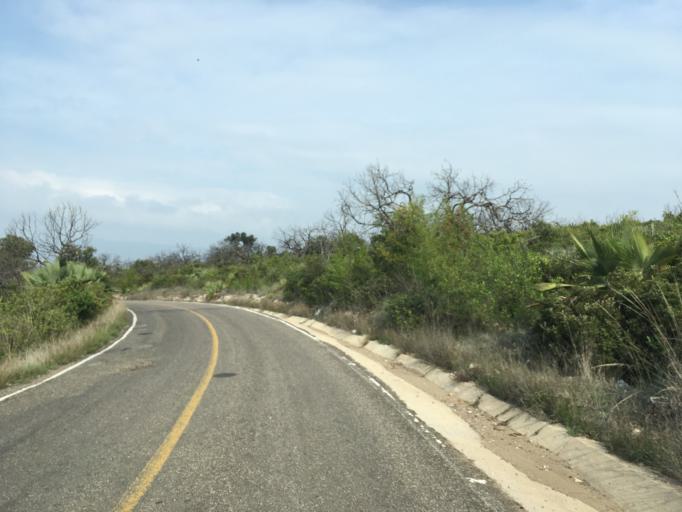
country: MX
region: Oaxaca
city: Magdalena Zahuatlan
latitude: 17.3722
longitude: -97.2114
